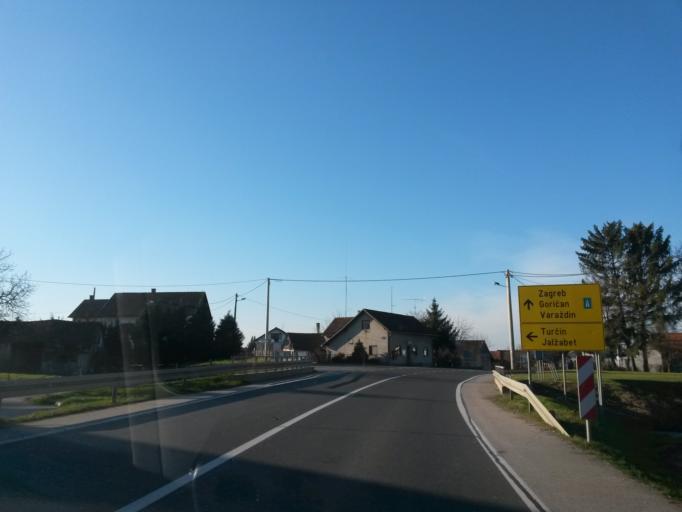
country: HR
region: Varazdinska
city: Jalzabet
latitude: 46.2636
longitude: 16.5212
